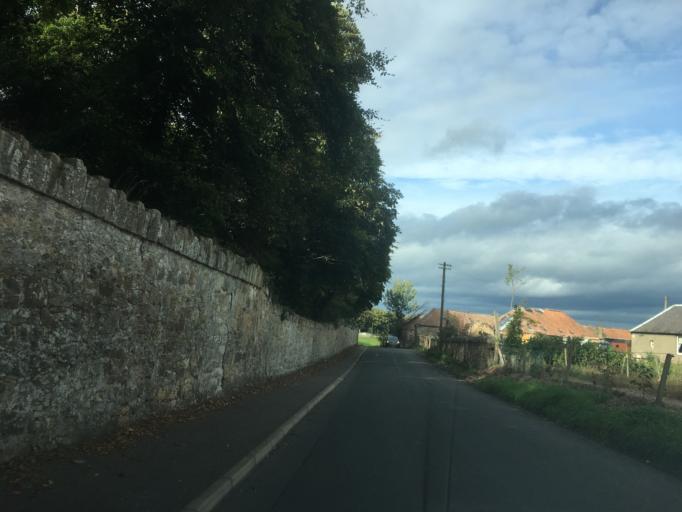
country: GB
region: Scotland
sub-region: East Lothian
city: Musselburgh
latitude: 55.9225
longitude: -3.0429
